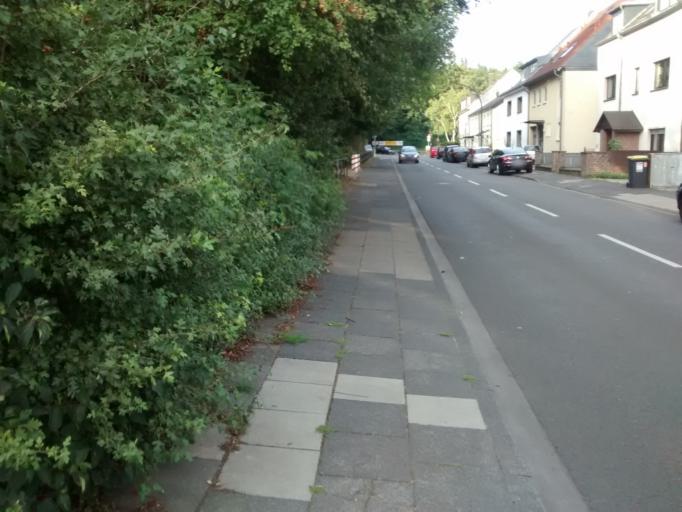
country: DE
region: North Rhine-Westphalia
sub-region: Regierungsbezirk Koln
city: Merheim
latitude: 50.9762
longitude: 7.0502
